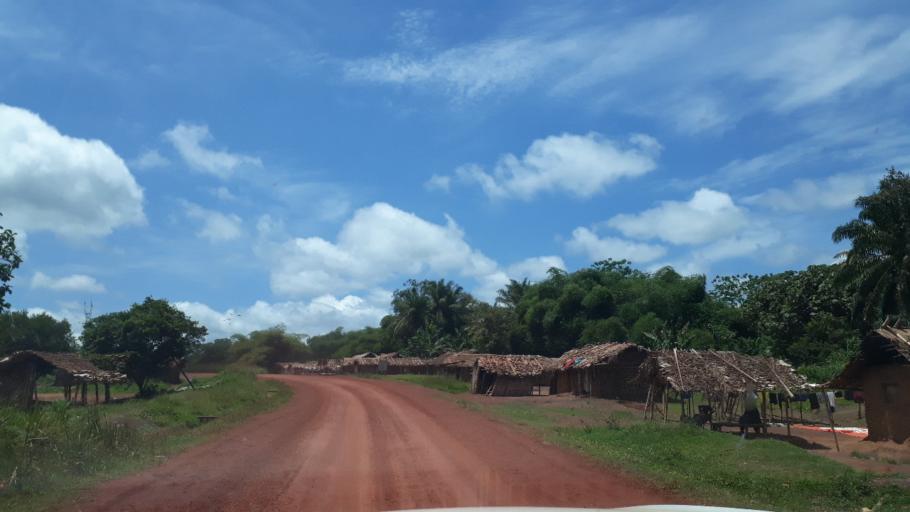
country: CD
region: Eastern Province
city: Kisangani
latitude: 0.5410
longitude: 25.9049
